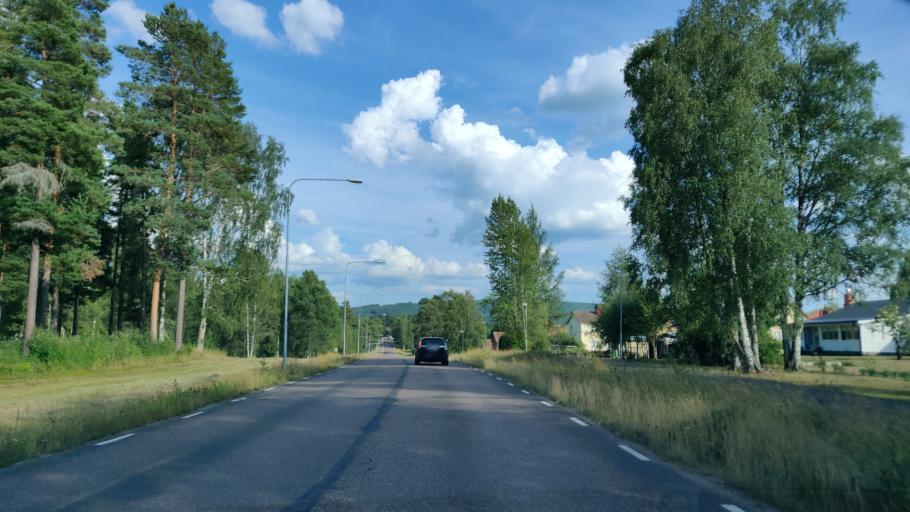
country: SE
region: Vaermland
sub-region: Hagfors Kommun
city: Hagfors
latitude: 60.0463
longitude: 13.6755
